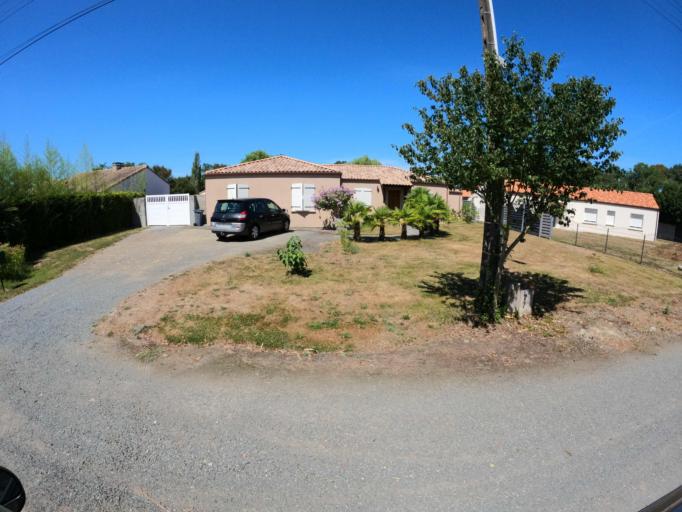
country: FR
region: Pays de la Loire
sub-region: Departement de la Loire-Atlantique
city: La Limouziniere
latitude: 46.9520
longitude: -1.6080
